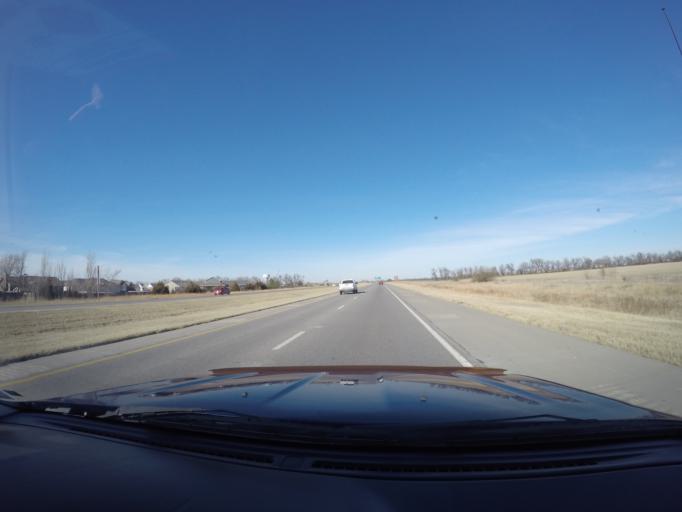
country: US
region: Kansas
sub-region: Harvey County
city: Newton
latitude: 38.0189
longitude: -97.3278
